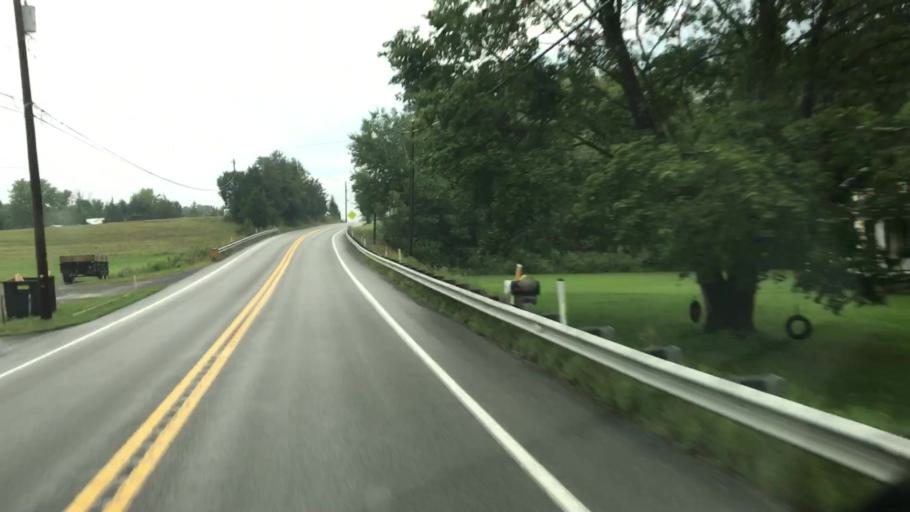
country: US
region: Pennsylvania
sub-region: Perry County
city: New Bloomfield
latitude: 40.3733
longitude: -77.1572
